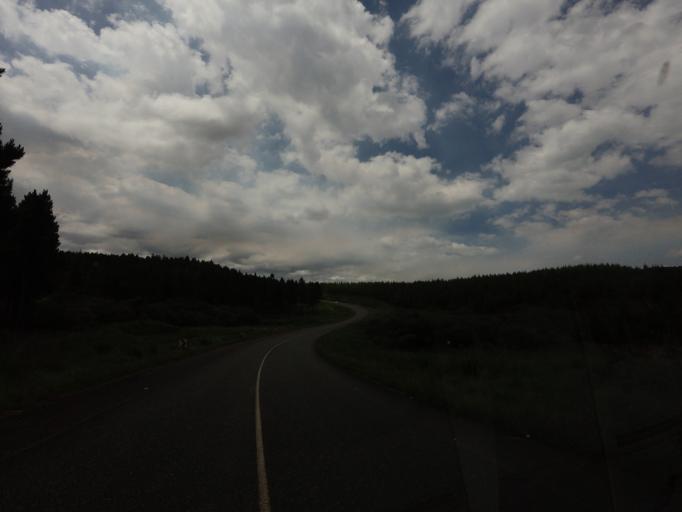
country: ZA
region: Mpumalanga
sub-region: Ehlanzeni District
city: Graksop
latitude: -24.9657
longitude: 30.8119
